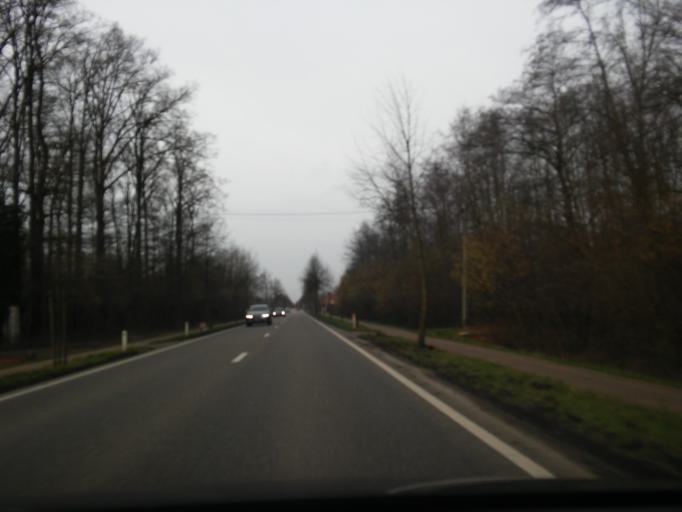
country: BE
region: Flanders
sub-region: Provincie Antwerpen
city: Herselt
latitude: 51.0660
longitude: 4.8807
